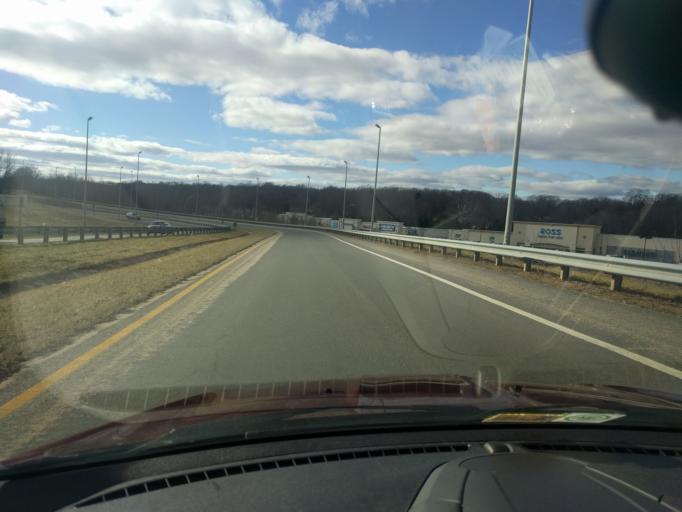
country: US
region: Virginia
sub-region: City of Lynchburg
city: West Lynchburg
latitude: 37.3421
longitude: -79.1920
